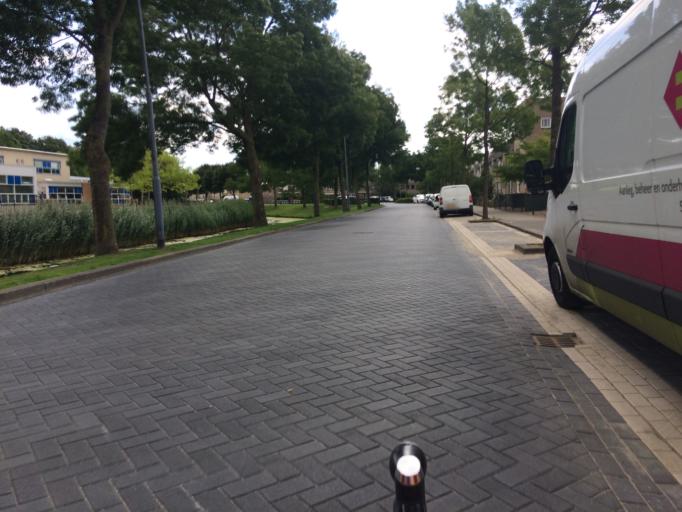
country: NL
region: Gelderland
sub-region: Gemeente Maasdriel
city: Hedel
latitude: 51.7301
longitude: 5.2878
